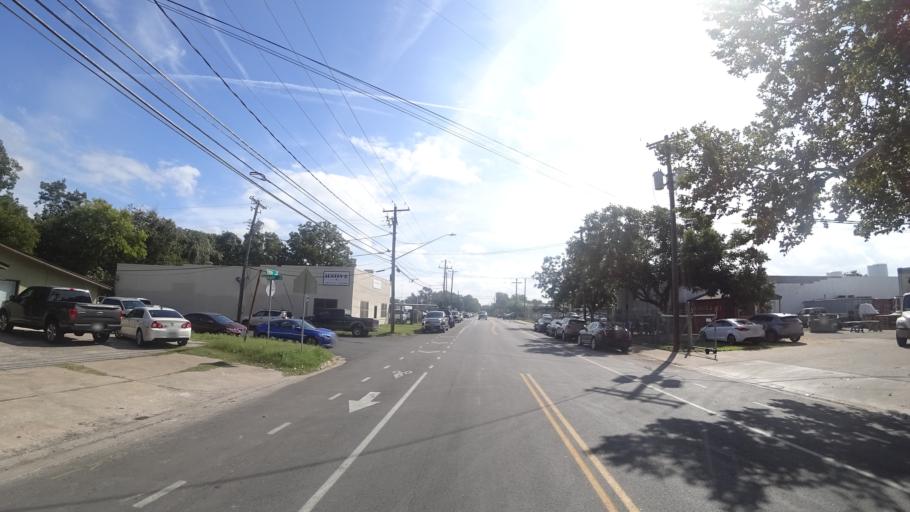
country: US
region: Texas
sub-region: Travis County
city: Austin
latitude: 30.2542
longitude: -97.7040
